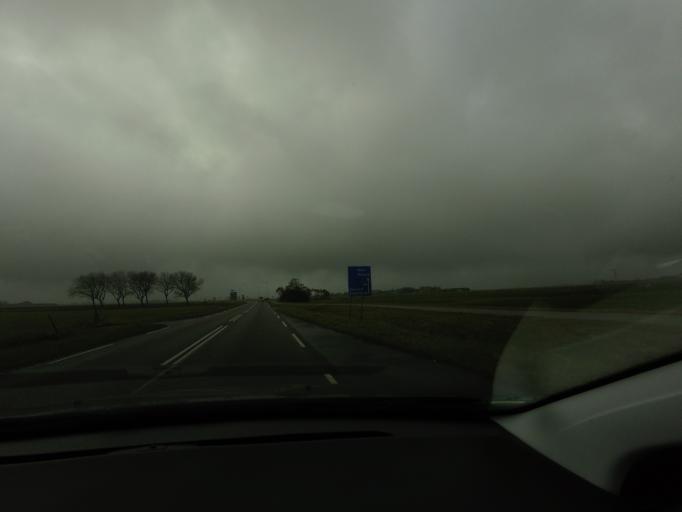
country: NL
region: Friesland
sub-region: Sudwest Fryslan
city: Makkum
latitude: 53.0869
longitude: 5.4396
